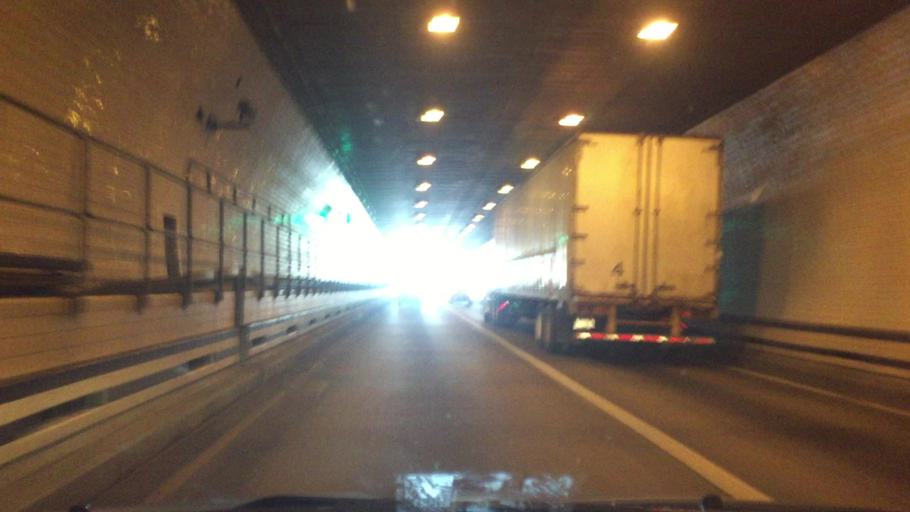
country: US
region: Virginia
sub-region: City of Newport News
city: Newport News
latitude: 36.9483
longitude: -76.4054
